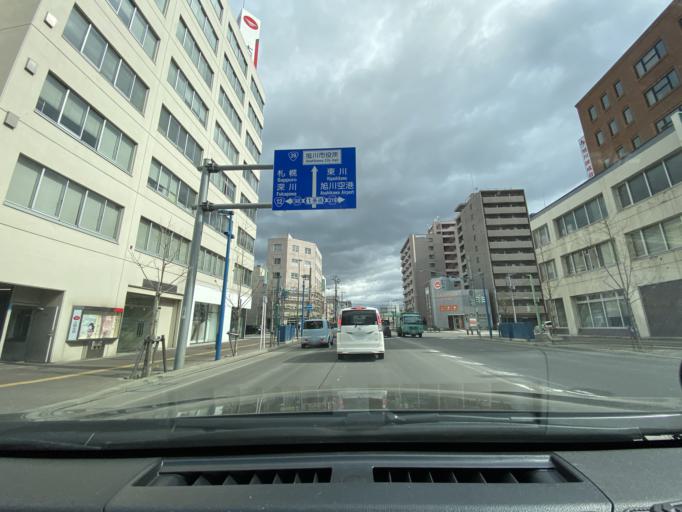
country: JP
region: Hokkaido
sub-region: Asahikawa-shi
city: Asahikawa
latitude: 43.7643
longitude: 142.3619
